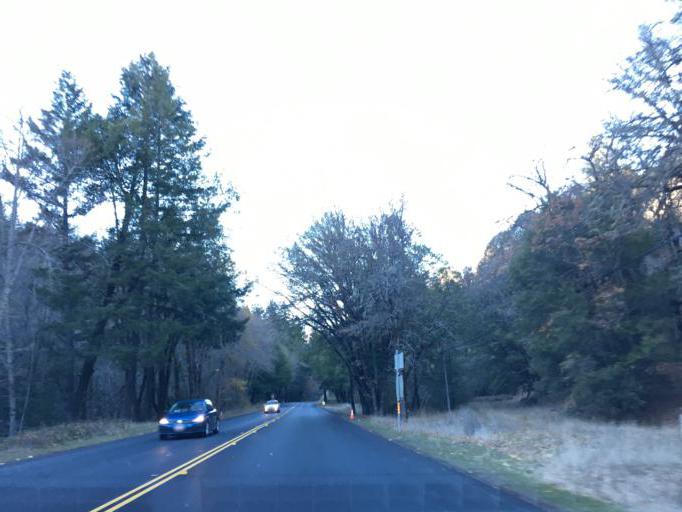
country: US
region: California
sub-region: Mendocino County
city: Laytonville
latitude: 39.8123
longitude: -123.5573
